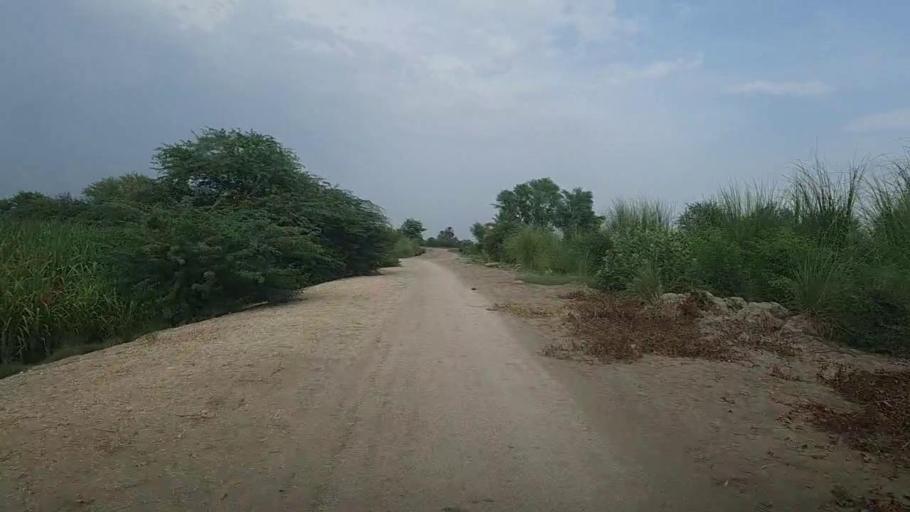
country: PK
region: Sindh
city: Karaundi
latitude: 26.9769
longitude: 68.4332
